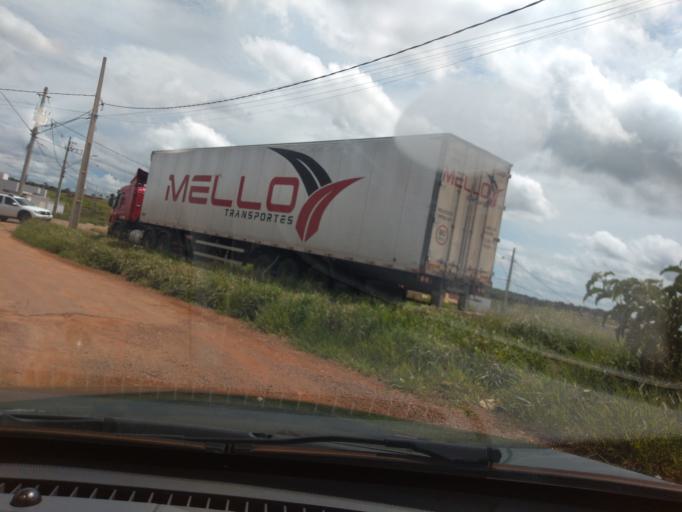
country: BR
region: Minas Gerais
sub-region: Tres Coracoes
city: Tres Coracoes
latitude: -21.6767
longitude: -45.2780
